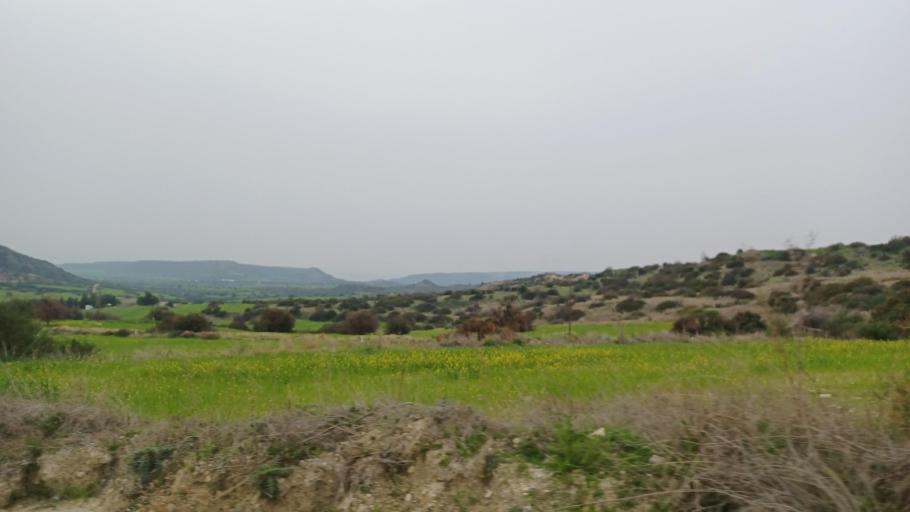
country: CY
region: Limassol
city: Pissouri
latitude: 34.7055
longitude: 32.7466
